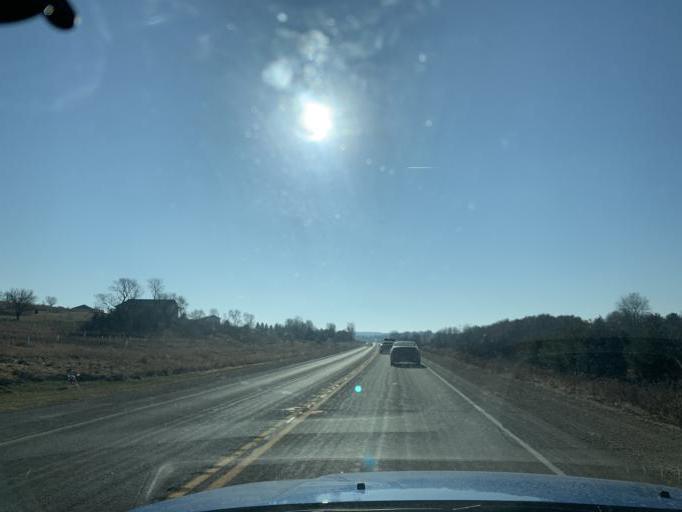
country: US
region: Wisconsin
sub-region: Green County
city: New Glarus
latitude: 42.8366
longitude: -89.6350
